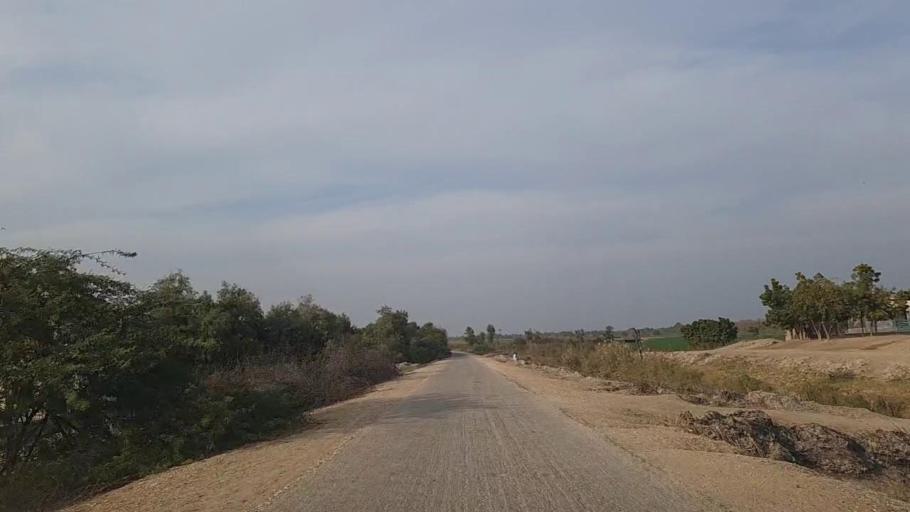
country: PK
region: Sindh
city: Daur
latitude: 26.4835
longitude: 68.4640
